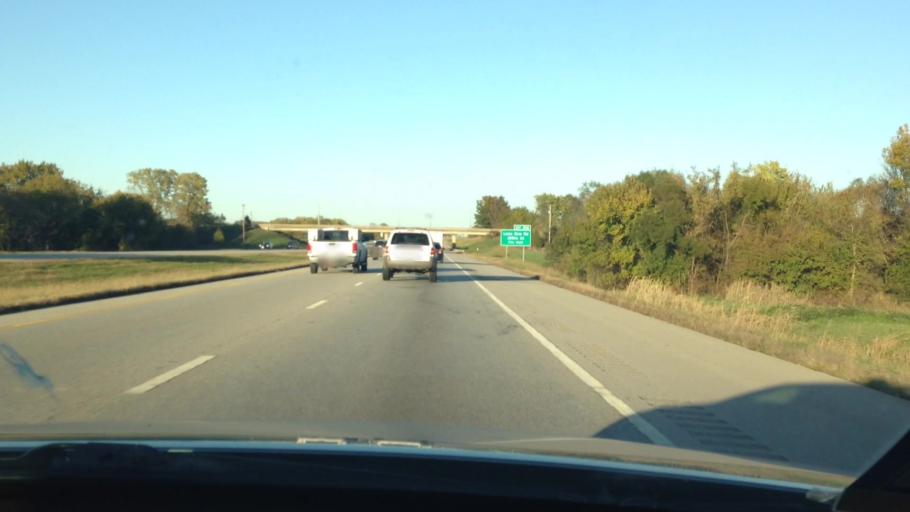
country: US
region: Kansas
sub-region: Johnson County
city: Gardner
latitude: 38.8236
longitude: -94.8610
